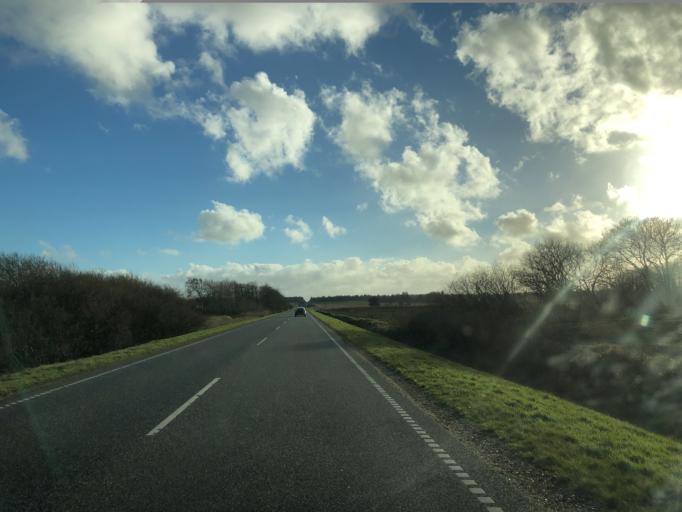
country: DK
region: Central Jutland
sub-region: Herning Kommune
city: Vildbjerg
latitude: 56.1911
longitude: 8.7113
